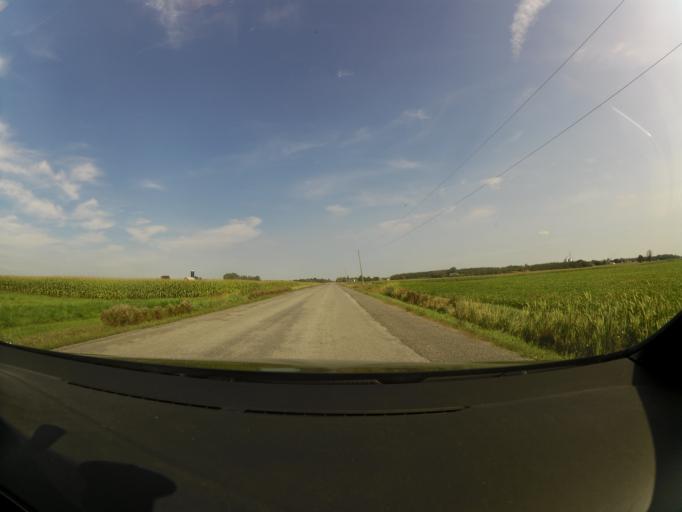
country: CA
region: Ontario
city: Carleton Place
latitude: 45.3126
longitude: -76.1953
